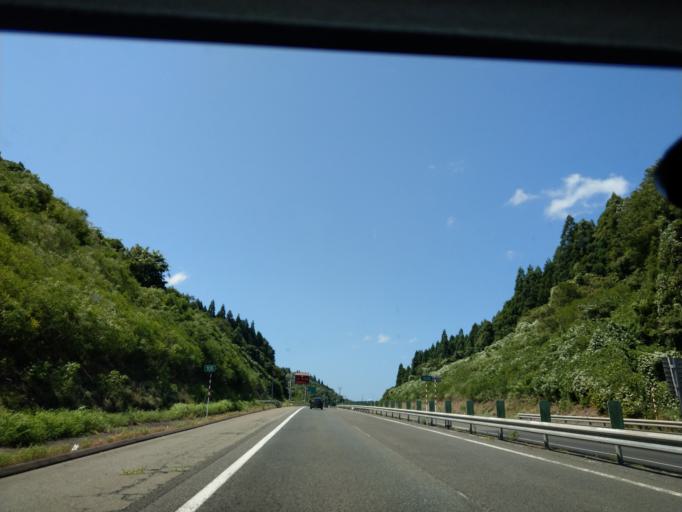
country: JP
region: Akita
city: Akita
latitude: 39.6561
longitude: 140.1980
